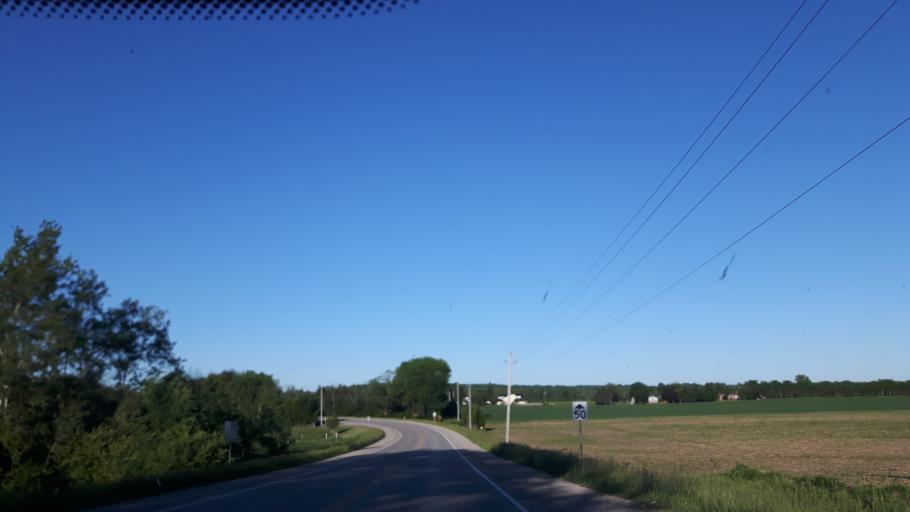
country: CA
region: Ontario
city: Goderich
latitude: 43.6428
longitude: -81.6105
